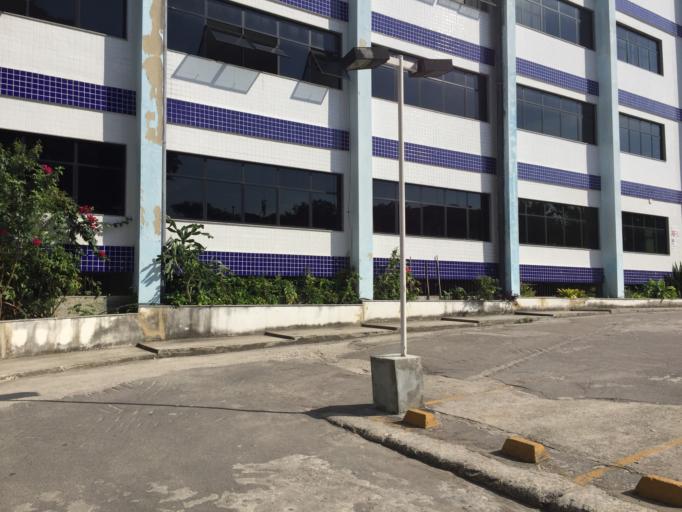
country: BR
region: Rio de Janeiro
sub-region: Rio De Janeiro
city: Rio de Janeiro
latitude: -22.9547
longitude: -43.1685
